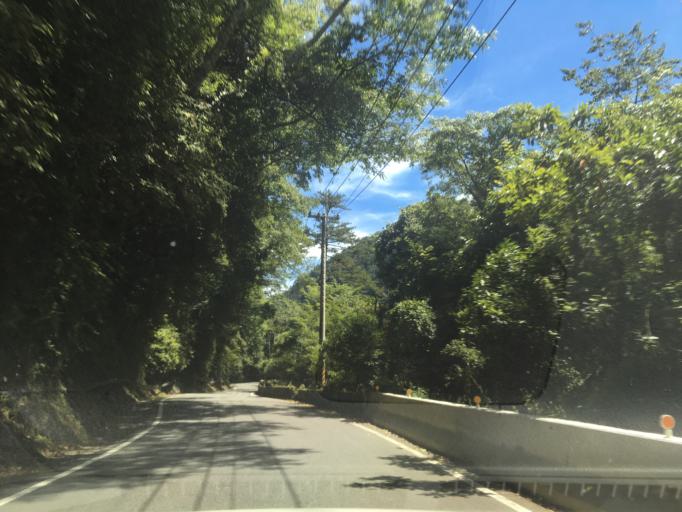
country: TW
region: Taiwan
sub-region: Nantou
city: Puli
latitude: 24.2149
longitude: 121.2655
